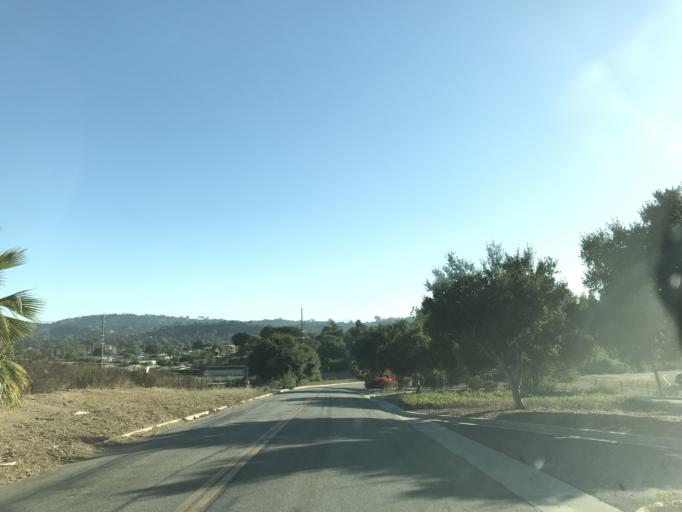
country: US
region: California
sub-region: Santa Barbara County
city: Mission Canyon
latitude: 34.4510
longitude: -119.7687
